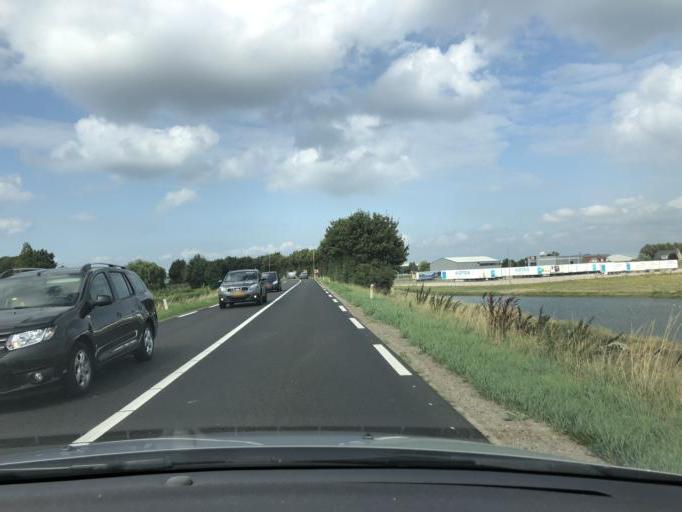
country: NL
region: Zeeland
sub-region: Gemeente Reimerswaal
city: Yerseke
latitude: 51.4736
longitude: 4.0486
